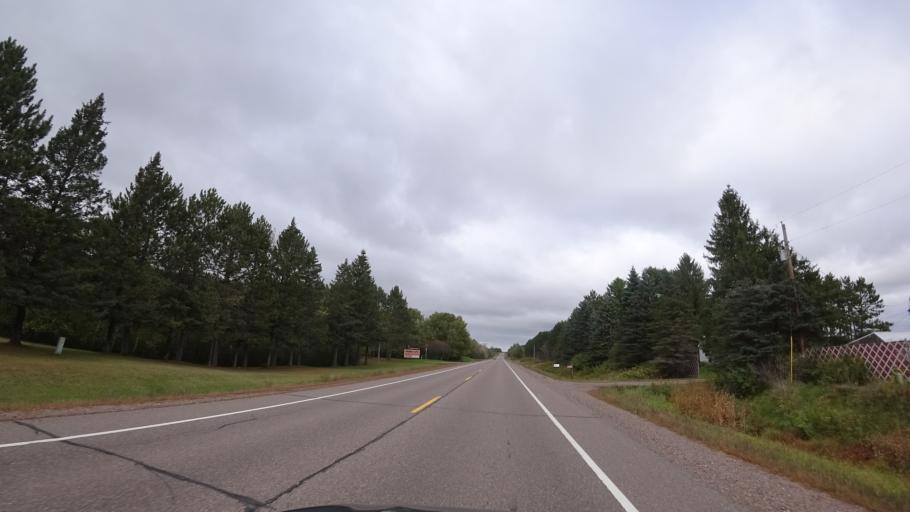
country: US
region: Wisconsin
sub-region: Rusk County
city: Ladysmith
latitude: 45.5257
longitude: -91.1115
